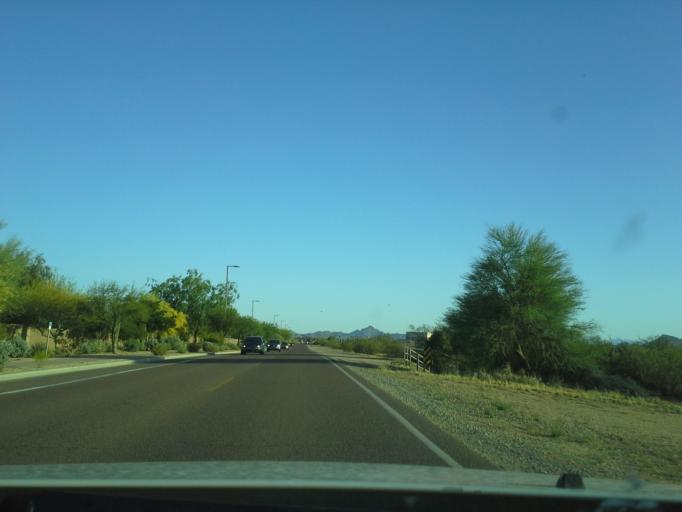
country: US
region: Arizona
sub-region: Maricopa County
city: Cave Creek
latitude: 33.6889
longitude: -112.0051
